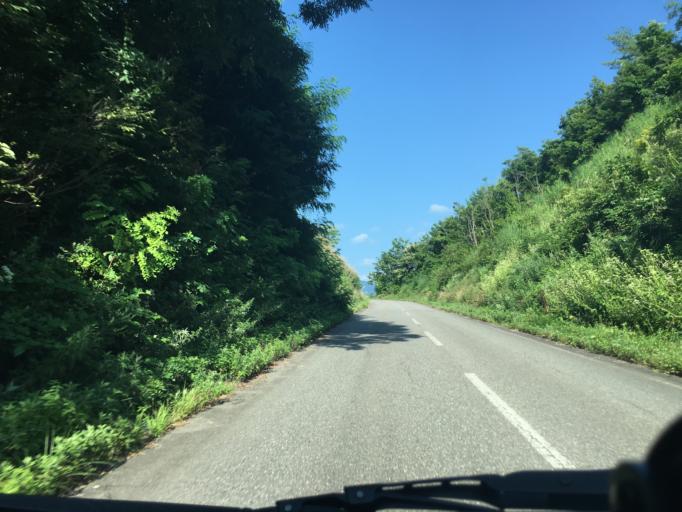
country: JP
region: Fukushima
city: Kitakata
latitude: 37.7391
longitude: 139.8715
